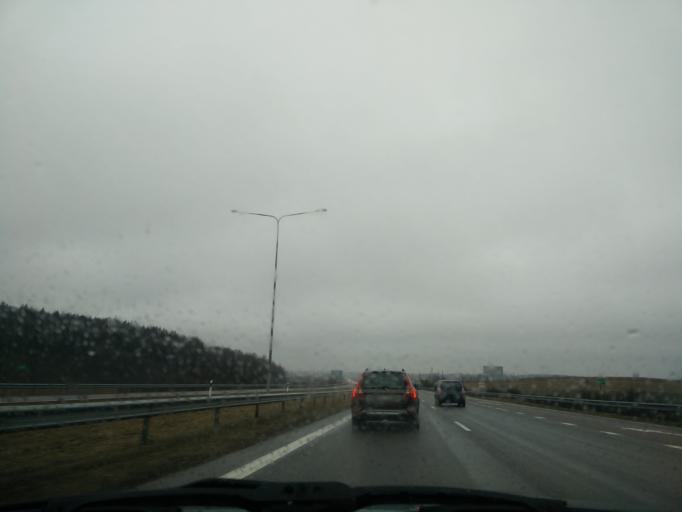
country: LT
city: Skaudvile
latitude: 55.4684
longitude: 22.6716
